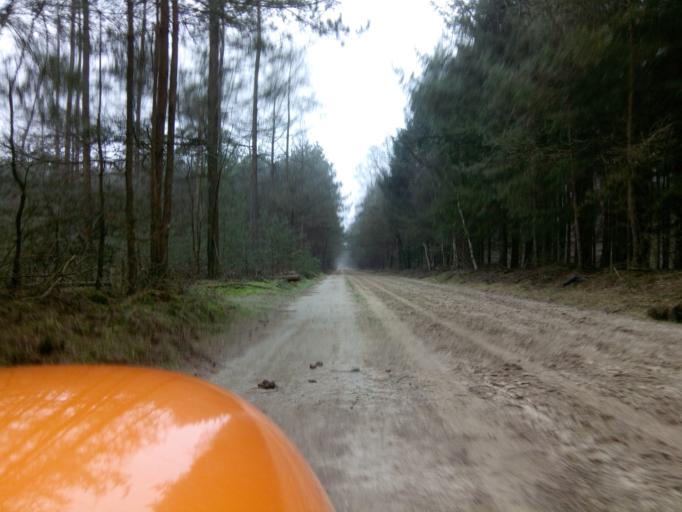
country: NL
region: Gelderland
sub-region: Gemeente Barneveld
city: Voorthuizen
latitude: 52.2181
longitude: 5.6429
